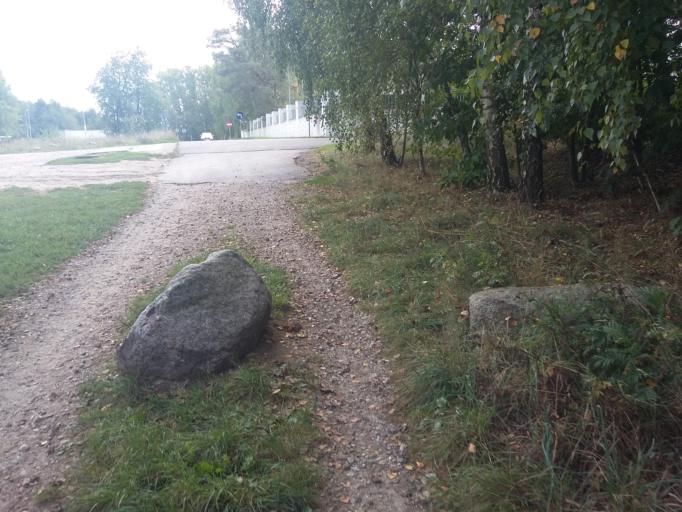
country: PL
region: Lodz Voivodeship
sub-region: Powiat pabianicki
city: Ksawerow
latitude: 51.7293
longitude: 19.3935
